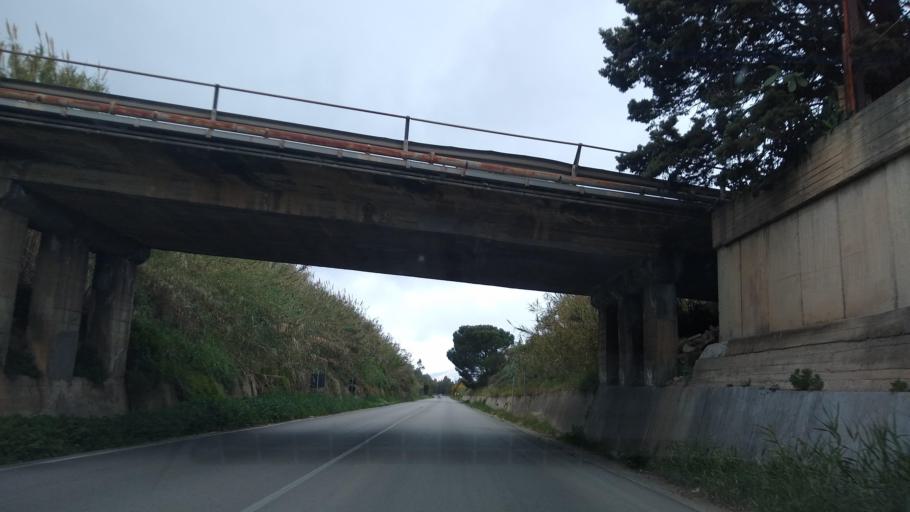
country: IT
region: Sicily
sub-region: Trapani
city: Alcamo
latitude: 37.9924
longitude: 12.9595
